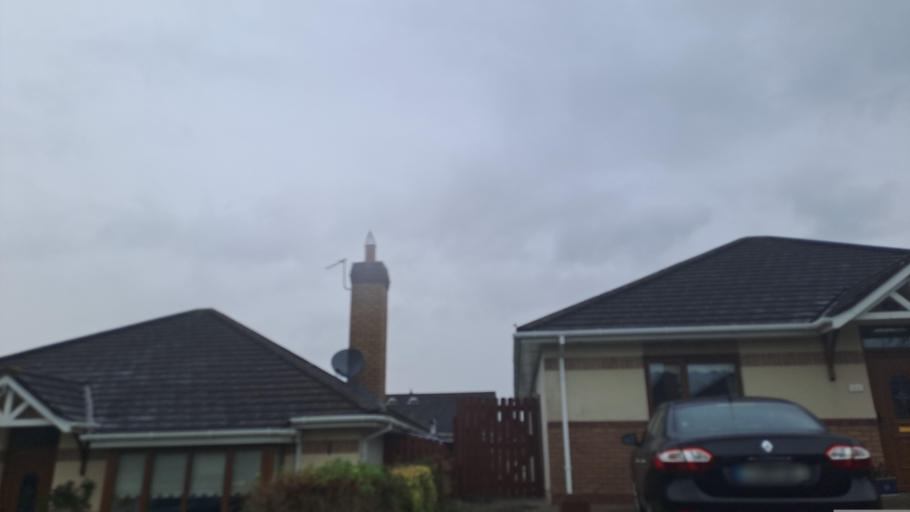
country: IE
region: Ulster
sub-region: An Cabhan
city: Virginia
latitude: 53.8381
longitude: -7.0755
